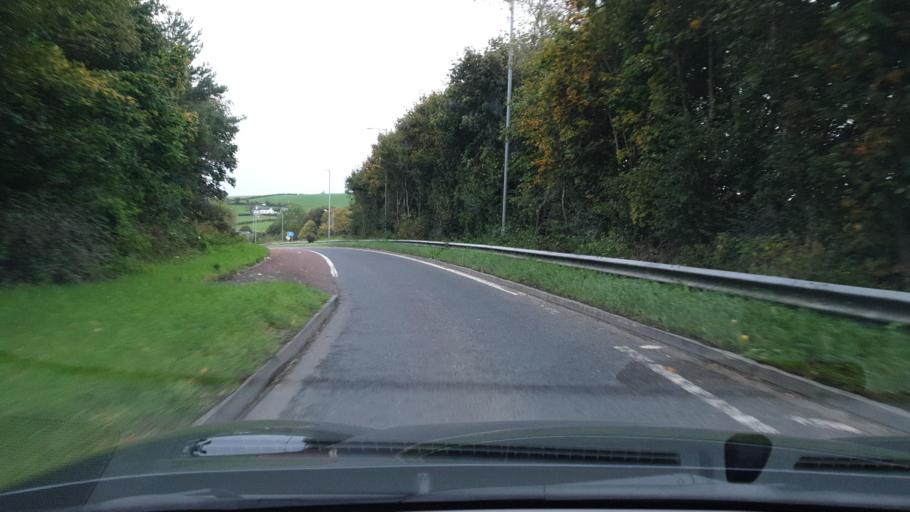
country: GB
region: Northern Ireland
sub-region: Banbridge District
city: Banbridge
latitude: 54.3302
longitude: -6.2834
